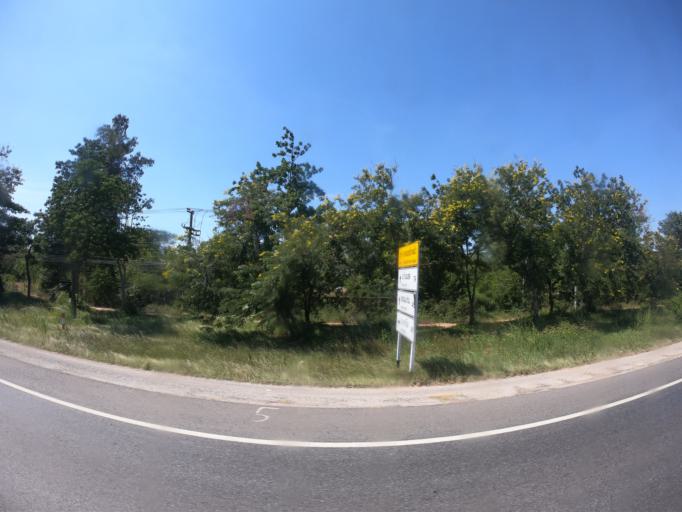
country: TH
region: Khon Kaen
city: Ban Phai
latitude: 16.0359
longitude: 102.7125
